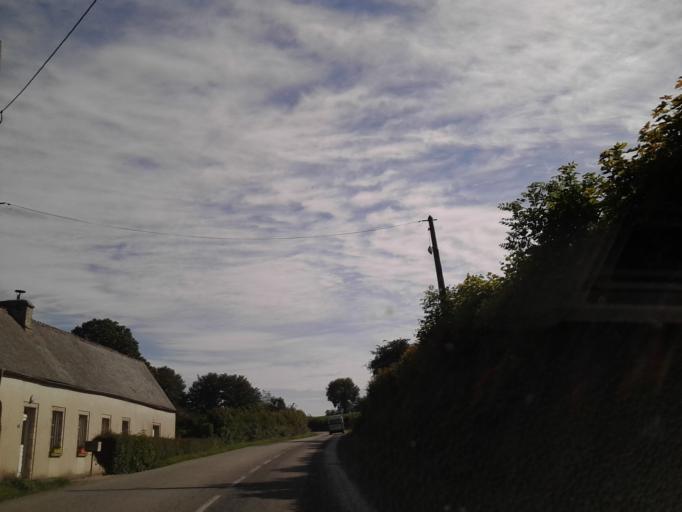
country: FR
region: Lower Normandy
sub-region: Departement de la Manche
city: Valognes
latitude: 49.5657
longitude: -1.4585
